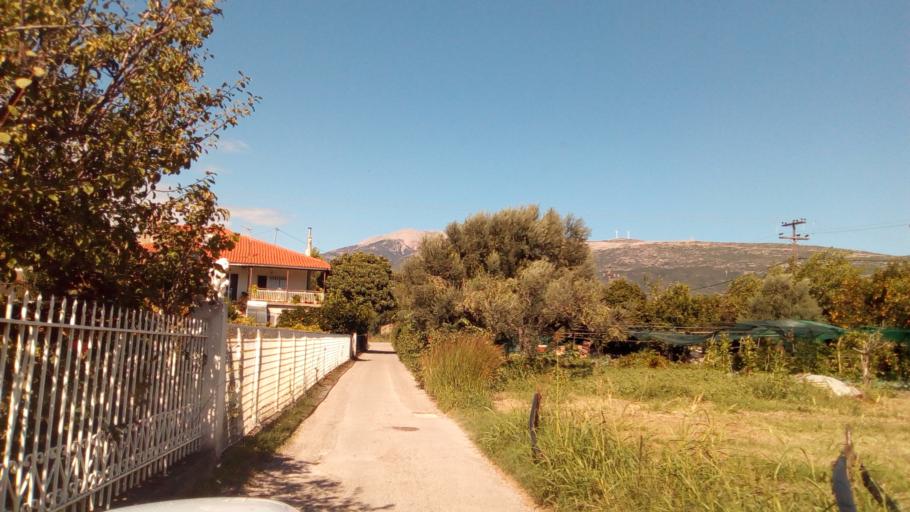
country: GR
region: West Greece
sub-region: Nomos Aitolias kai Akarnanias
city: Nafpaktos
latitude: 38.3791
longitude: 21.7987
